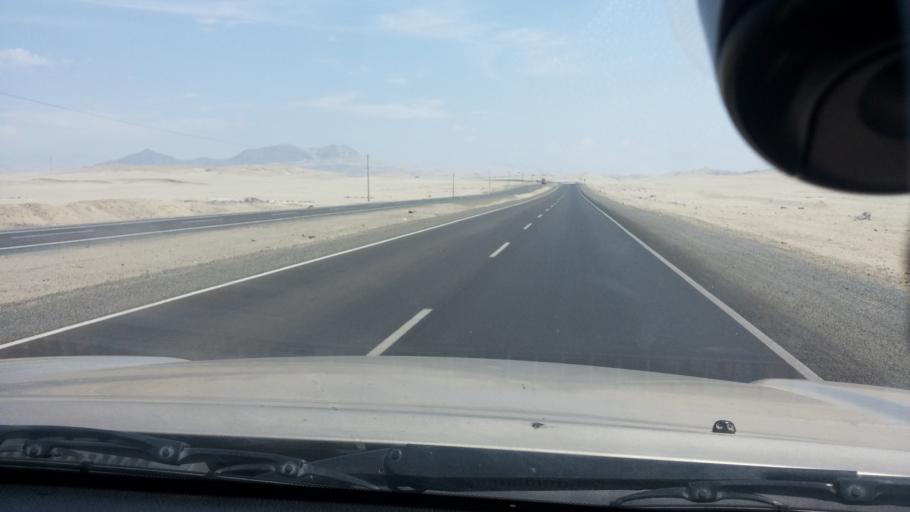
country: PE
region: Ancash
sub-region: Provincia de Casma
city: Casma
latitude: -9.5439
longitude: -78.2723
